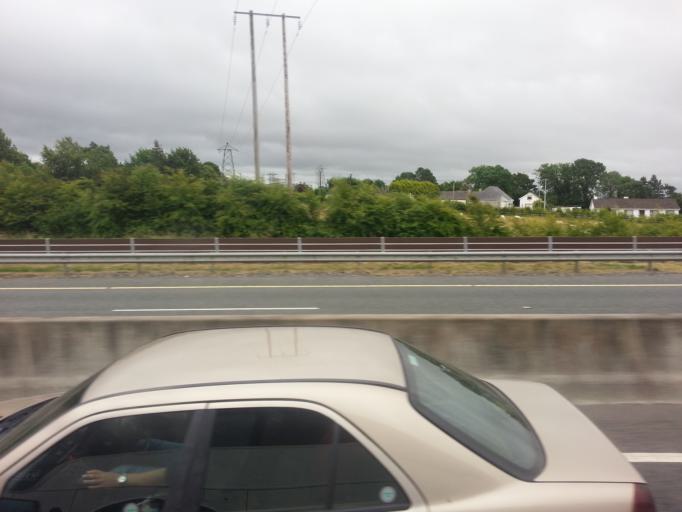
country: IE
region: Leinster
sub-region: Kildare
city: Castledermot
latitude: 52.8328
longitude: -6.8480
